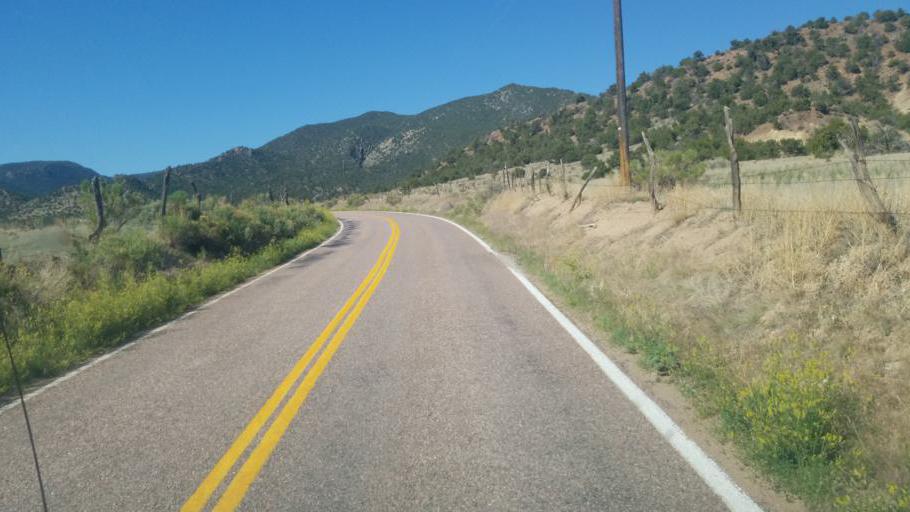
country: US
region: Colorado
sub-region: Fremont County
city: Canon City
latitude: 38.4382
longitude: -105.3795
